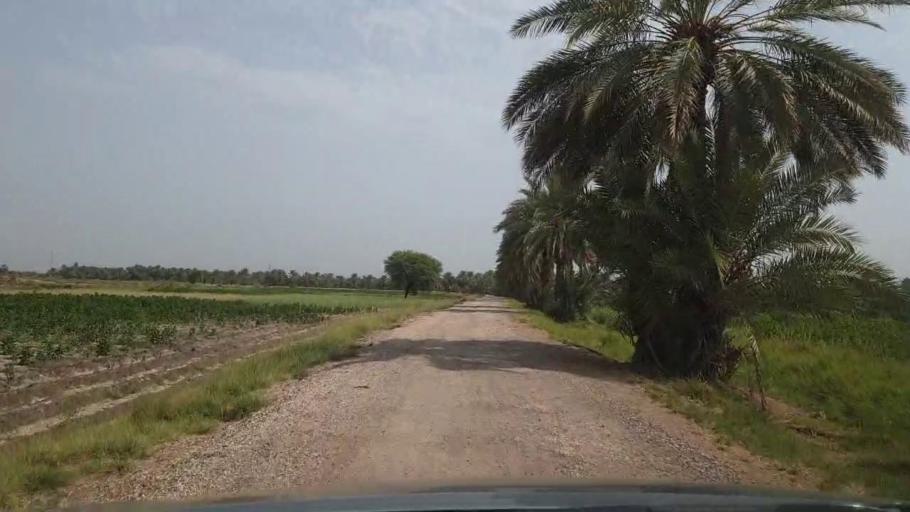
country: PK
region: Sindh
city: Rohri
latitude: 27.6826
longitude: 69.0359
